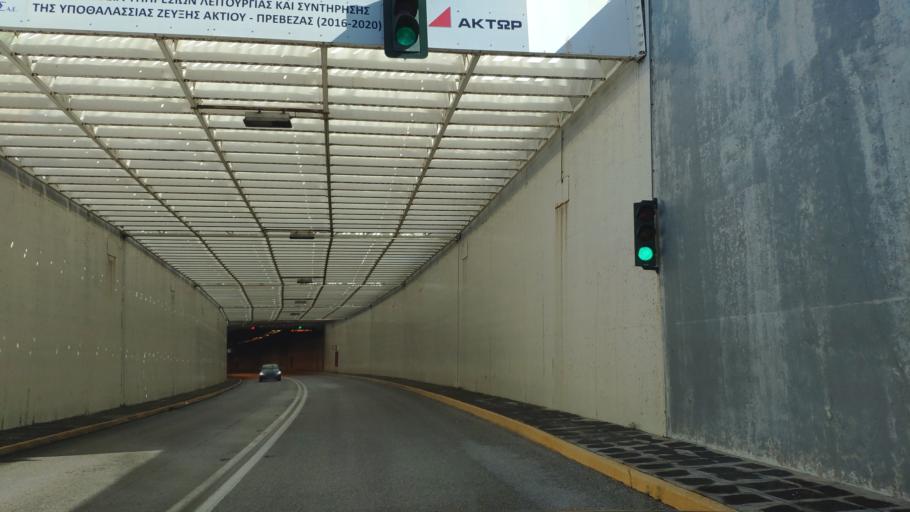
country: GR
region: Epirus
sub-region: Nomos Prevezis
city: Preveza
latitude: 38.9439
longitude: 20.7641
